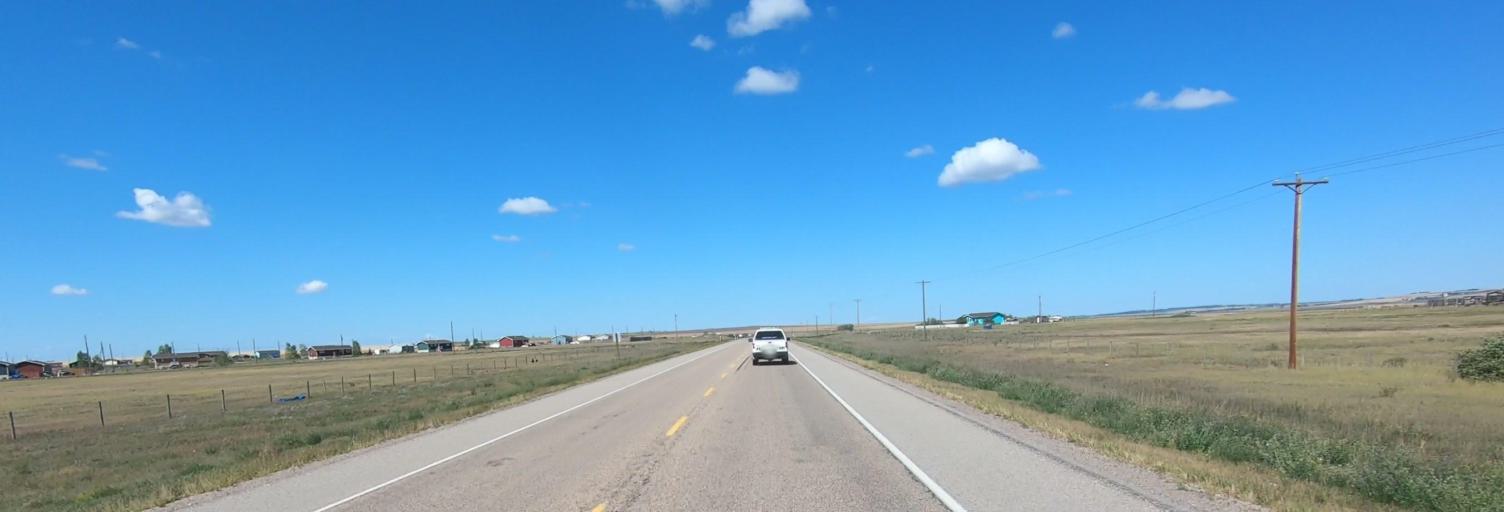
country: CA
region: Alberta
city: Strathmore
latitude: 50.8869
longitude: -113.1865
